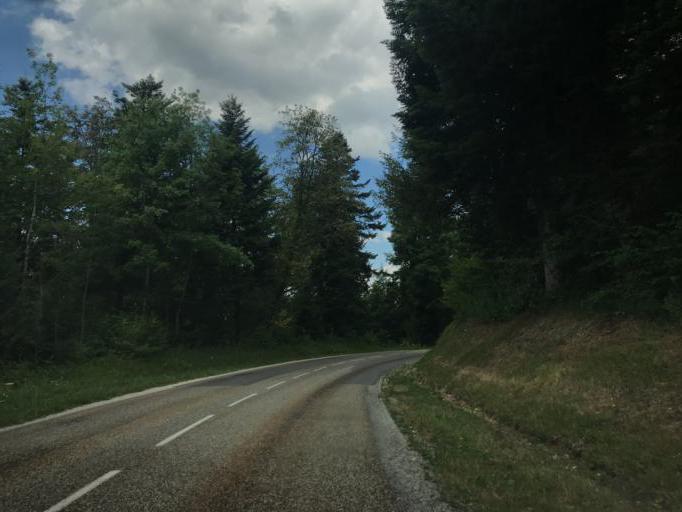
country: FR
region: Franche-Comte
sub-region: Departement du Jura
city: Clairvaux-les-Lacs
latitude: 46.5519
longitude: 5.7789
